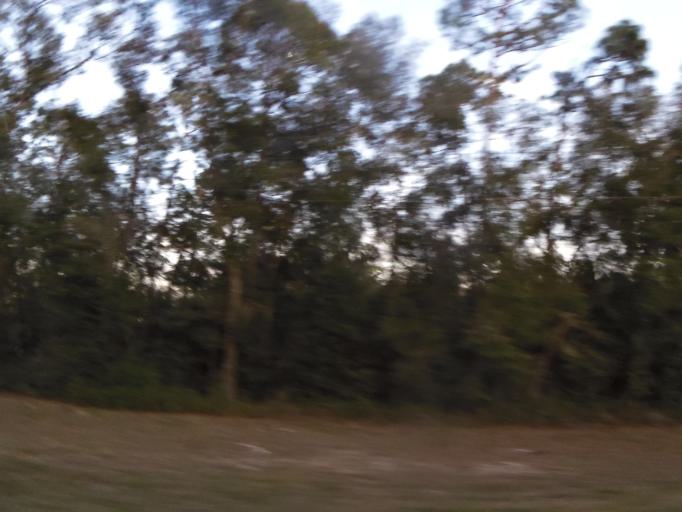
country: US
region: Florida
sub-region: Volusia County
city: De Leon Springs
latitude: 29.1352
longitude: -81.2849
